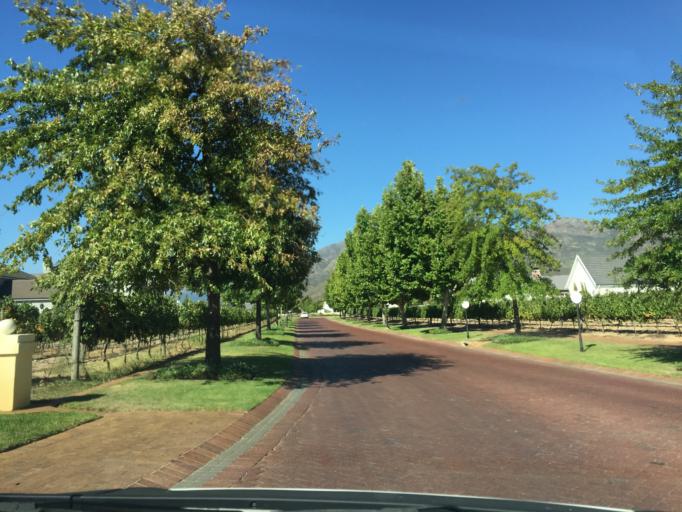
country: ZA
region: Western Cape
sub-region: Cape Winelands District Municipality
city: Paarl
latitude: -33.8022
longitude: 18.9675
